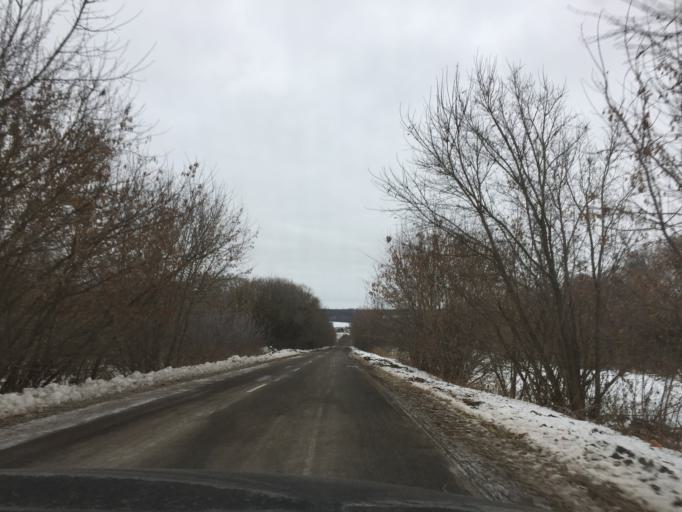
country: RU
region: Tula
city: Teploye
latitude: 53.7785
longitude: 37.6338
